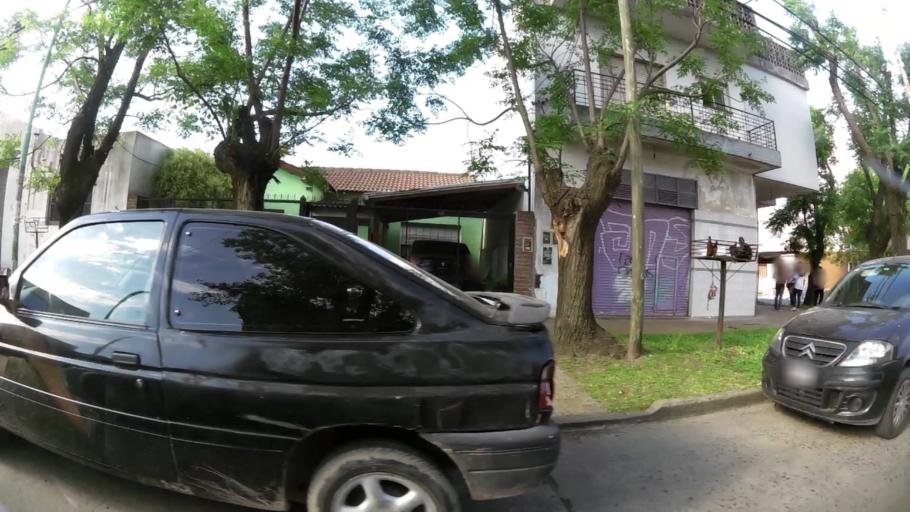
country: AR
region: Buenos Aires
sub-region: Partido de Merlo
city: Merlo
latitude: -34.6607
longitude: -58.7331
